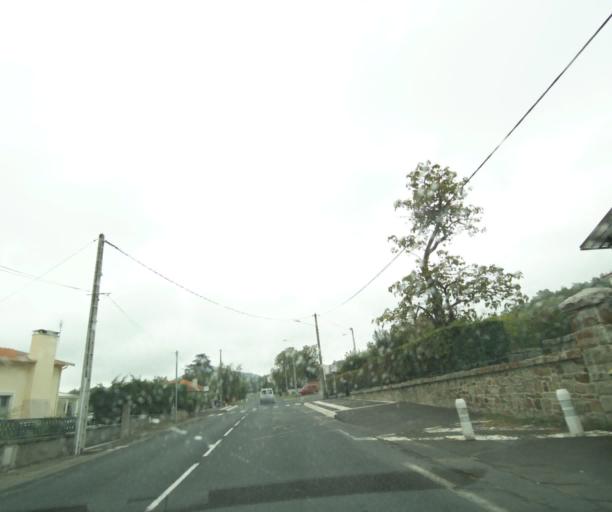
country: FR
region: Auvergne
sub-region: Departement du Puy-de-Dome
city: Ceyrat
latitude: 45.7234
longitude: 3.0672
